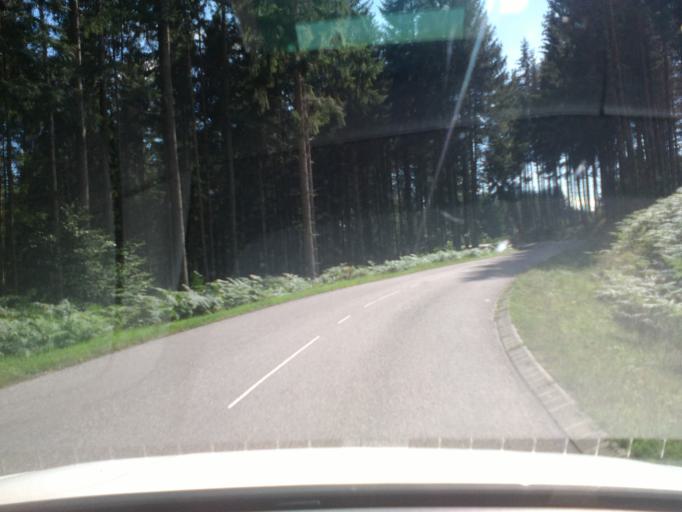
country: FR
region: Lorraine
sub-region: Departement des Vosges
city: Senones
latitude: 48.3665
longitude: 6.9768
